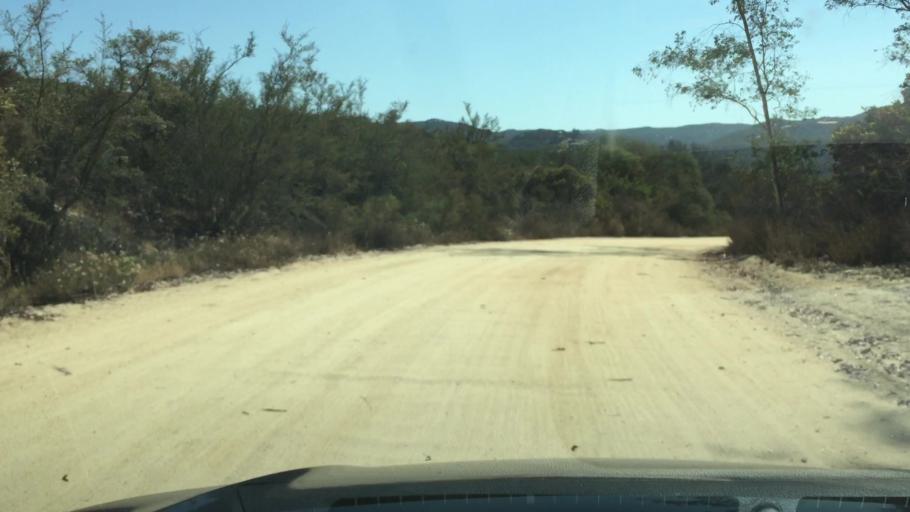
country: US
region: California
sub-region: San Diego County
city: Alpine
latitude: 32.7541
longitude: -116.7490
